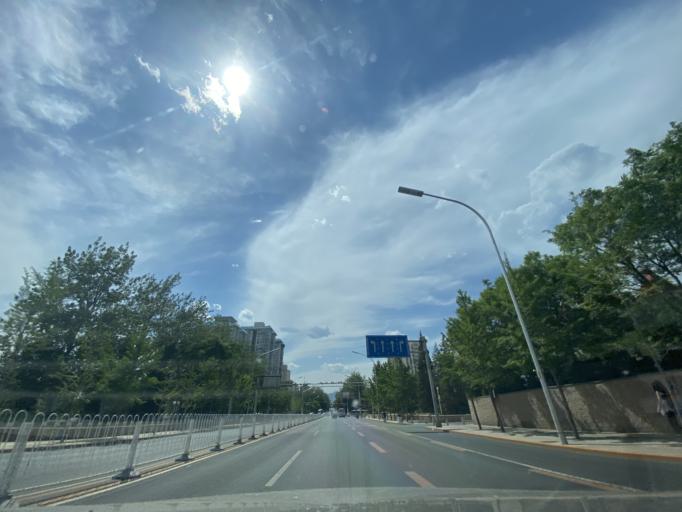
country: CN
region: Beijing
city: Lugu
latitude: 39.9062
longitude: 116.1950
